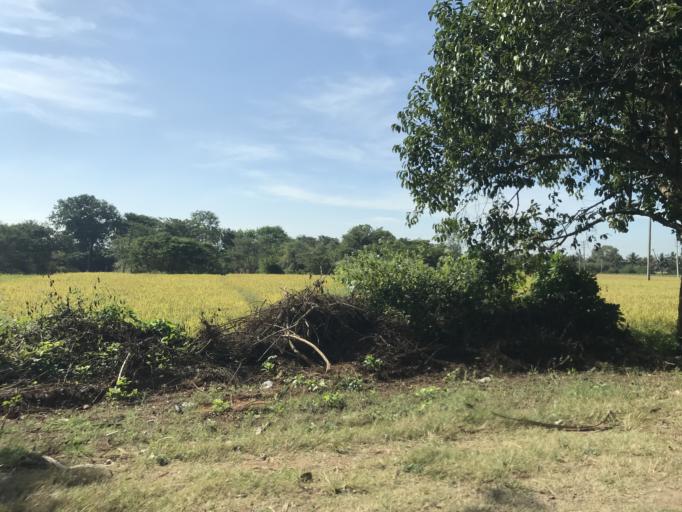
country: IN
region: Karnataka
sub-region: Mysore
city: Heggadadevankote
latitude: 12.1264
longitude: 76.4531
